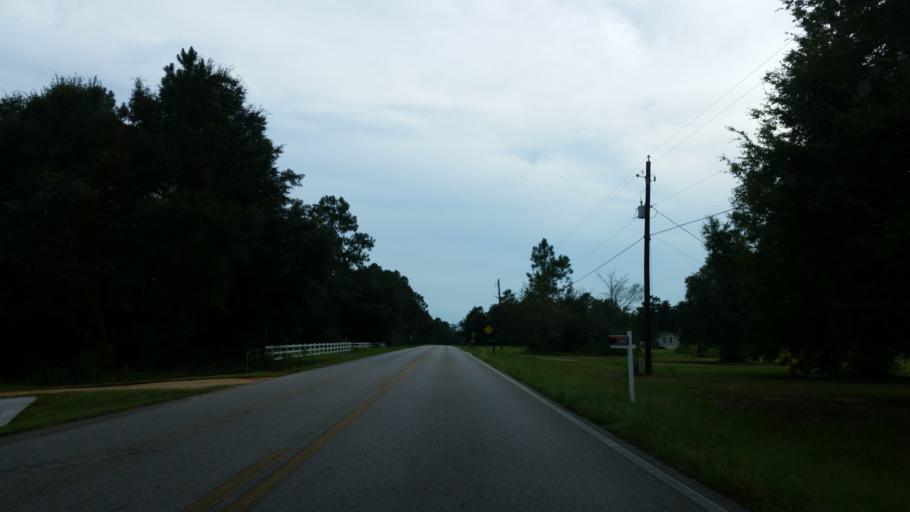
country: US
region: Florida
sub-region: Santa Rosa County
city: Point Baker
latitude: 30.6805
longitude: -86.9914
